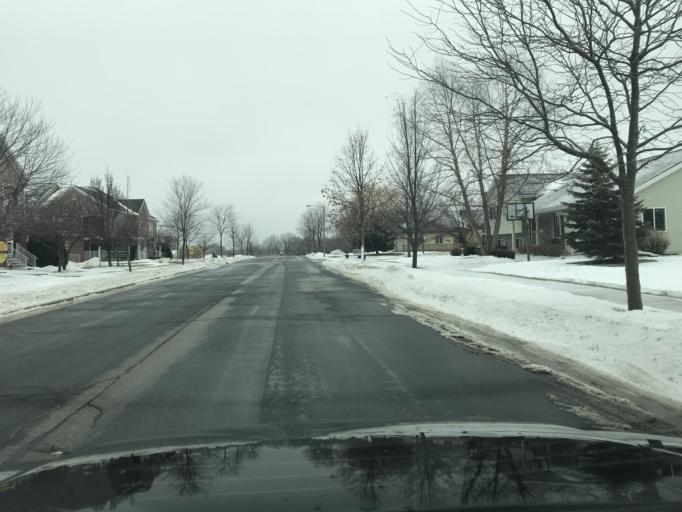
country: US
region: Wisconsin
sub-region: Dane County
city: Cottage Grove
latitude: 43.0902
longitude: -89.2149
